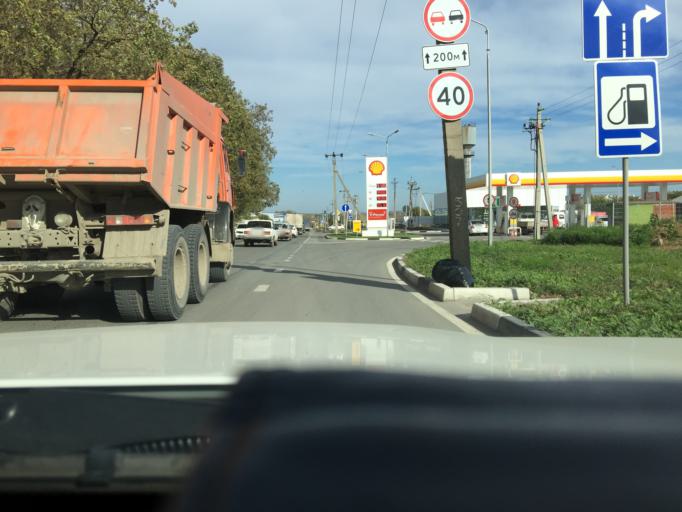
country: RU
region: Rostov
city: Imeni Chkalova
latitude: 47.2972
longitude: 39.8036
